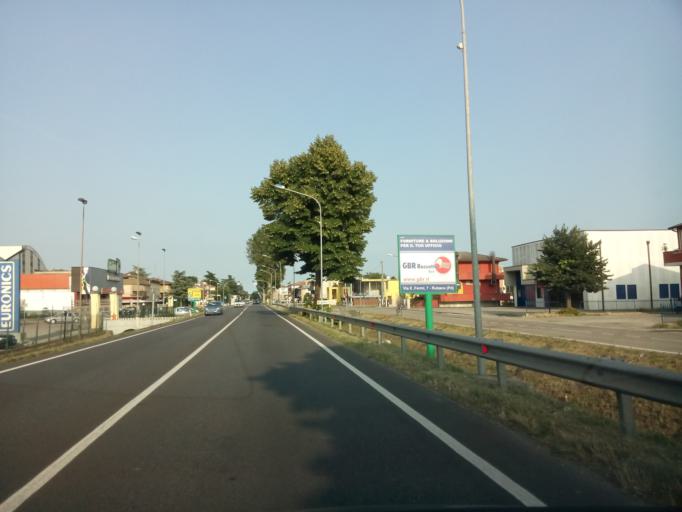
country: IT
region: Veneto
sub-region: Provincia di Padova
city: Sarmeola
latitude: 45.4222
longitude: 11.8044
